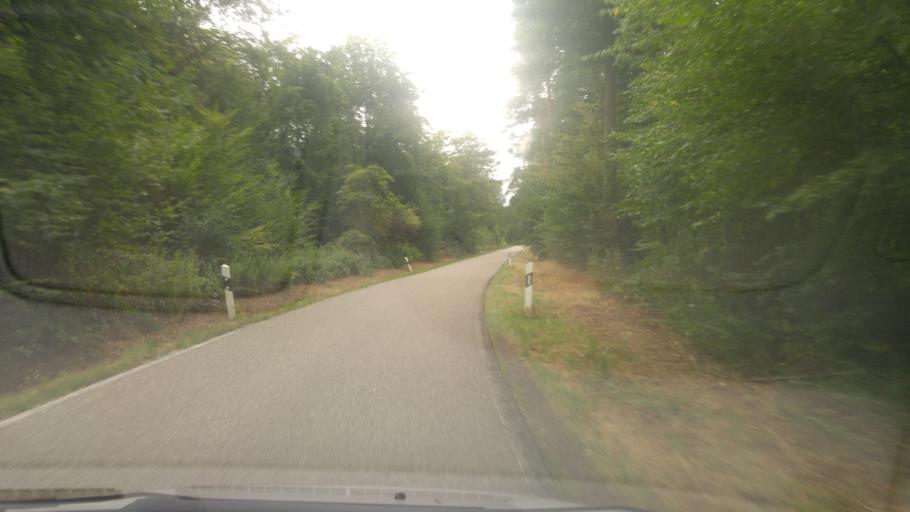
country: DE
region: Rheinland-Pfalz
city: Steinfeld
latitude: 49.0052
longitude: 8.0669
